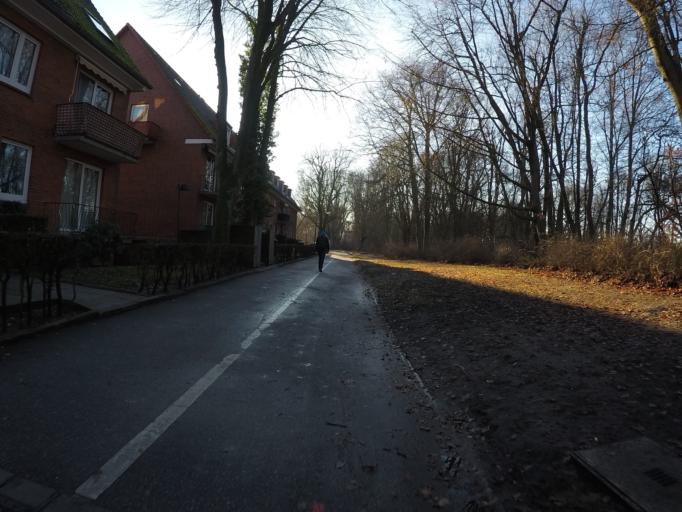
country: DE
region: Hamburg
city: Fuhlsbuettel
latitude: 53.6478
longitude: 10.0177
